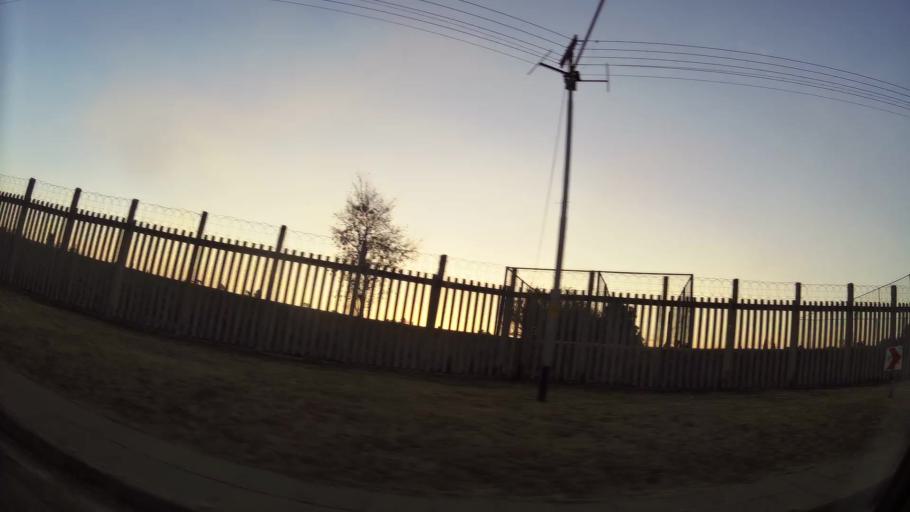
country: ZA
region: Gauteng
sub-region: Ekurhuleni Metropolitan Municipality
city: Germiston
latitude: -26.2684
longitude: 28.1619
